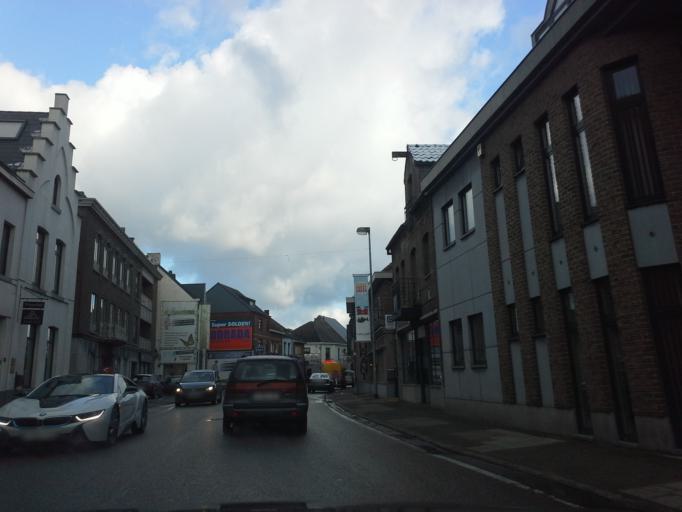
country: BE
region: Flanders
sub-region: Provincie Limburg
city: Neerpelt
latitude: 51.2292
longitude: 5.4365
